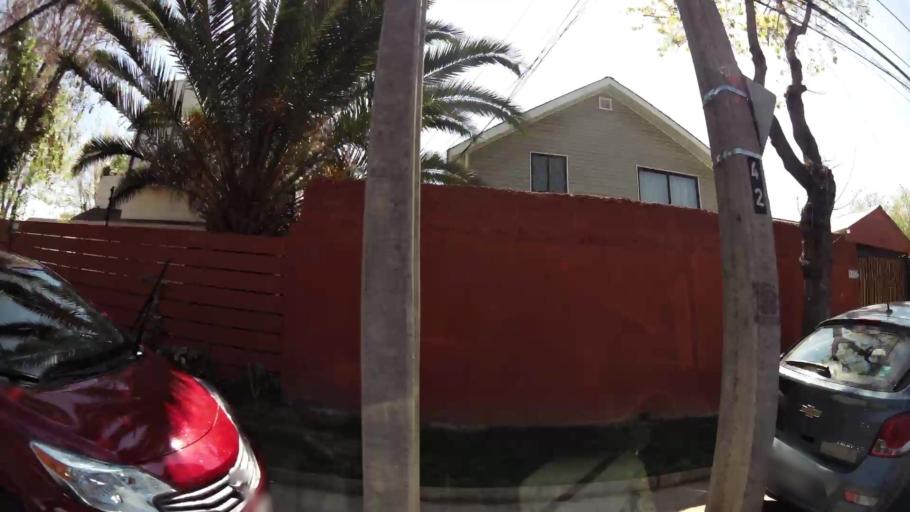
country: CL
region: Santiago Metropolitan
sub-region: Provincia de Santiago
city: Villa Presidente Frei, Nunoa, Santiago, Chile
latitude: -33.4279
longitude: -70.5456
